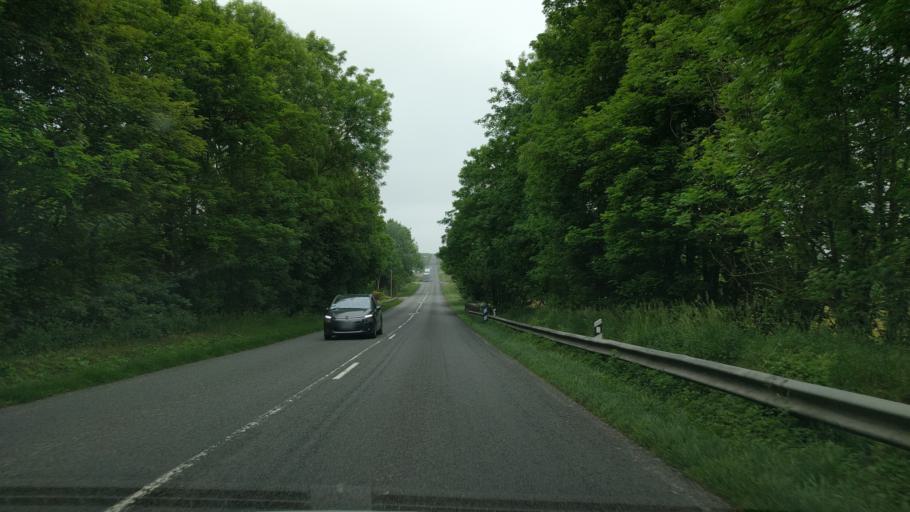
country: FR
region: Picardie
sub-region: Departement de la Somme
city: Peronne
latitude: 49.9529
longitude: 2.9274
